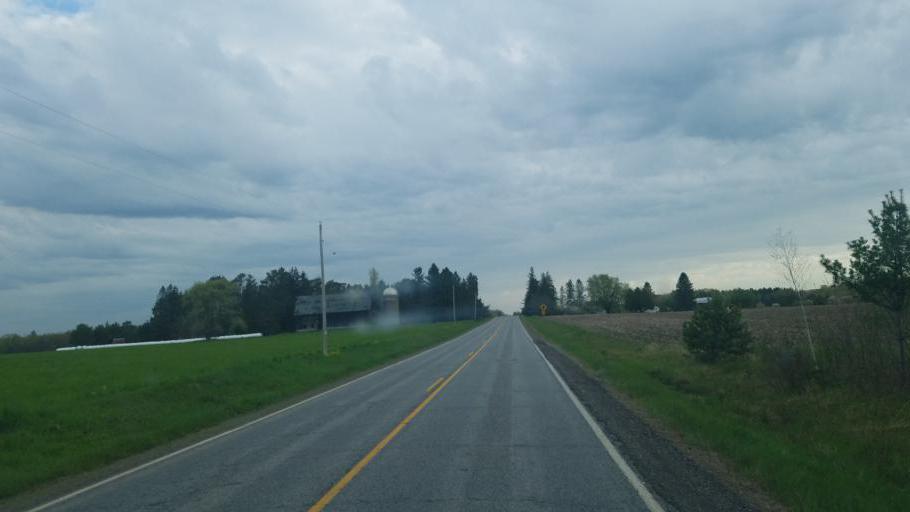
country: US
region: Wisconsin
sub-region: Wood County
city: Nekoosa
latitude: 44.3912
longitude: -90.1602
